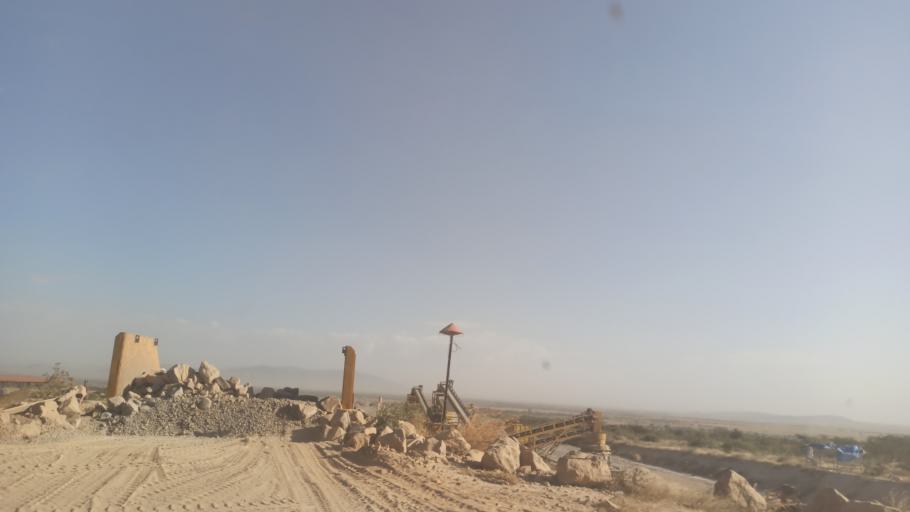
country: ET
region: Oromiya
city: Ziway
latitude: 7.9362
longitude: 38.6134
